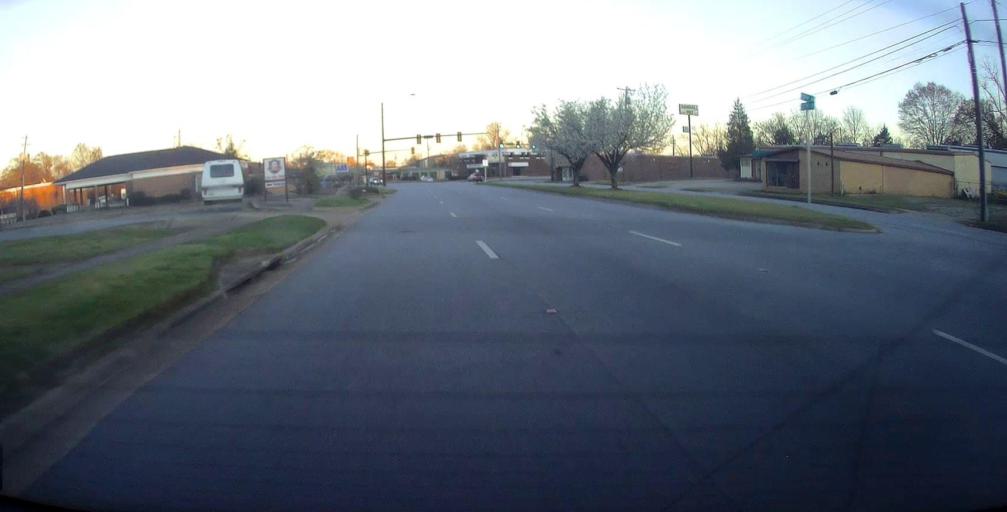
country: US
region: Alabama
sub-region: Russell County
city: Phenix City
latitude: 32.4713
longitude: -85.0058
